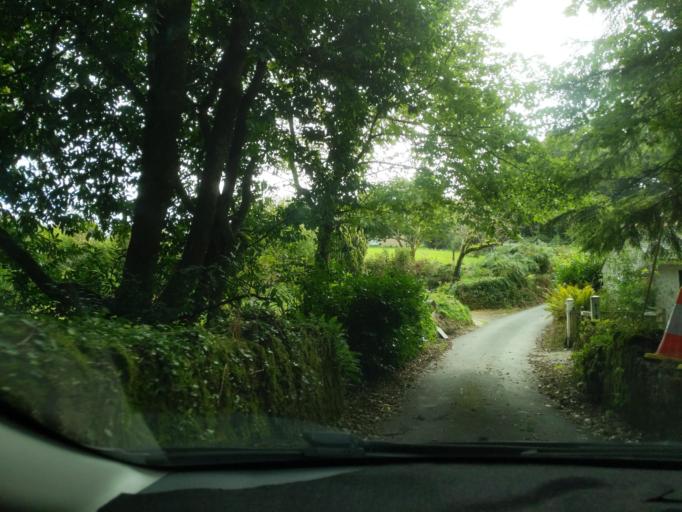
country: GB
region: England
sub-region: Cornwall
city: Lostwithiel
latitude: 50.3958
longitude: -4.7039
